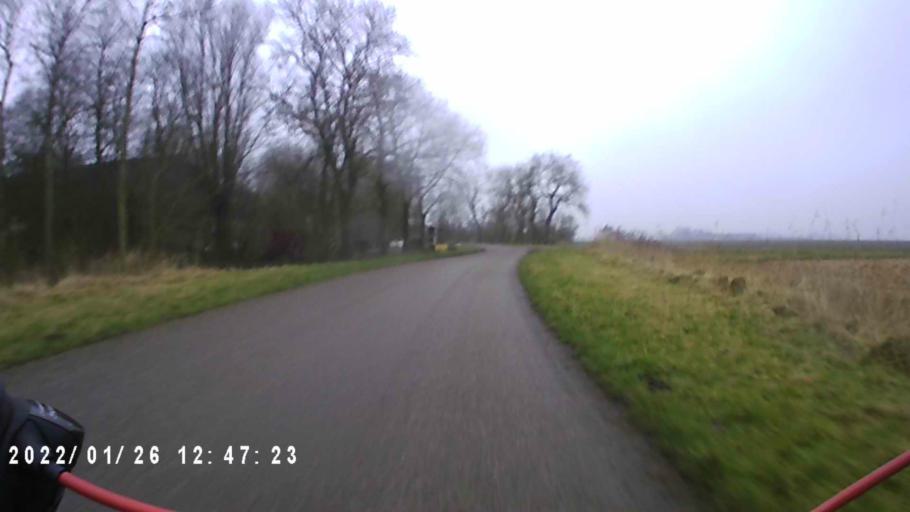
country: NL
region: Groningen
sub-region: Gemeente Winsum
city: Winsum
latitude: 53.3420
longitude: 6.4958
